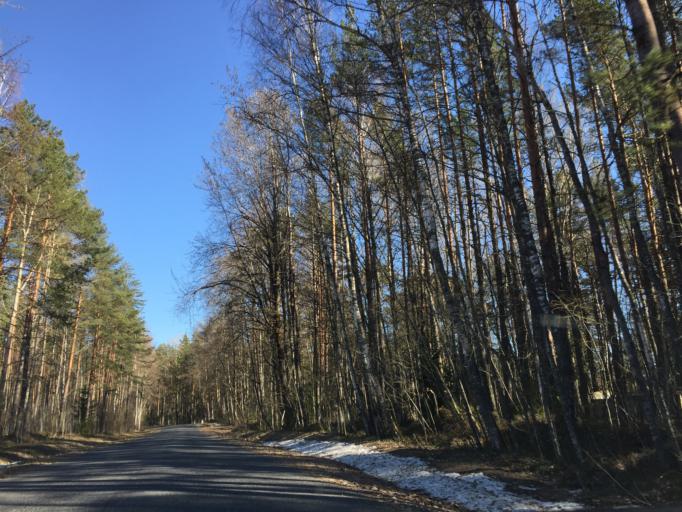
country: EE
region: Ida-Virumaa
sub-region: Johvi vald
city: Johvi
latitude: 59.0091
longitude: 27.4523
